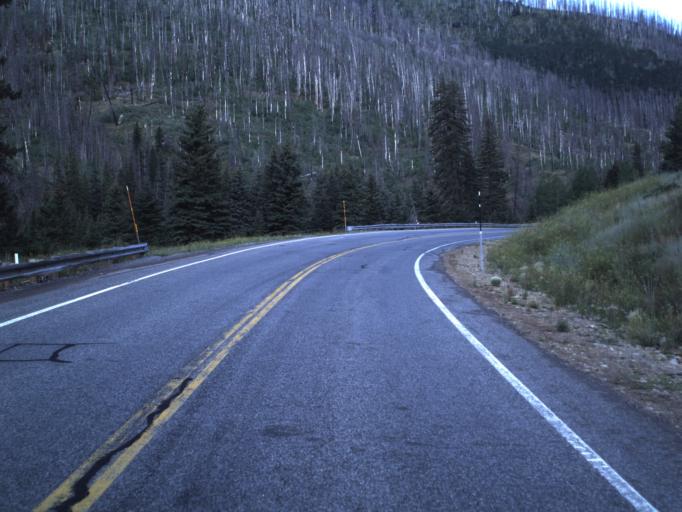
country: US
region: Utah
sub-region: Emery County
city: Huntington
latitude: 39.5375
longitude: -111.1587
